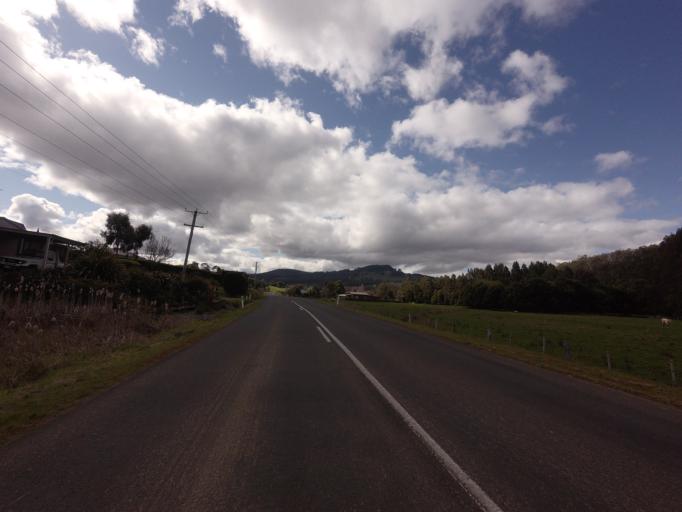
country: AU
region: Tasmania
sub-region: Huon Valley
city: Geeveston
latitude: -43.1742
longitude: 146.9239
